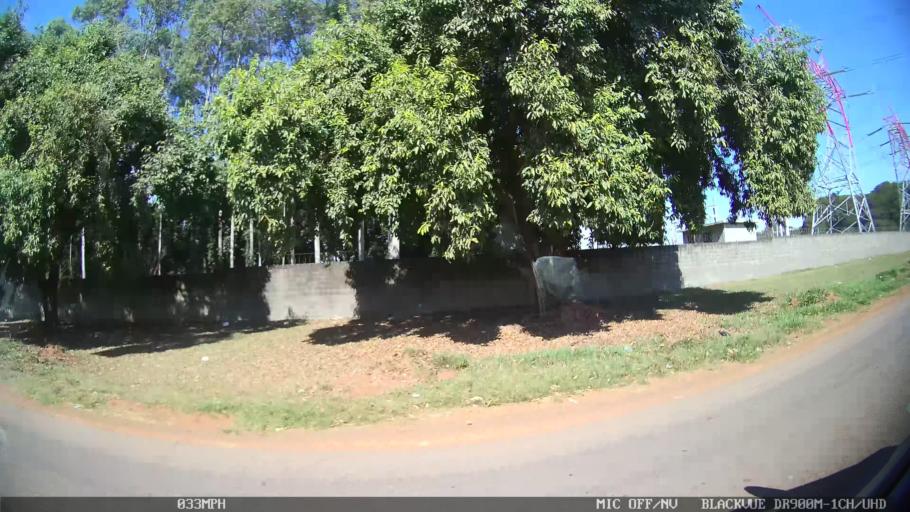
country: BR
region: Sao Paulo
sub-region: Santa Barbara D'Oeste
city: Santa Barbara d'Oeste
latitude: -22.7242
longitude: -47.4179
